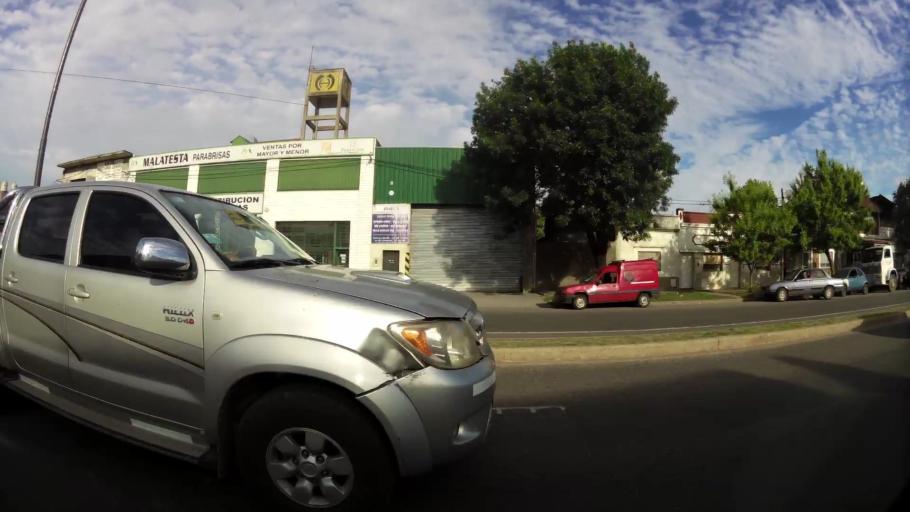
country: AR
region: Santa Fe
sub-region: Departamento de Rosario
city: Rosario
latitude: -32.9780
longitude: -60.6702
